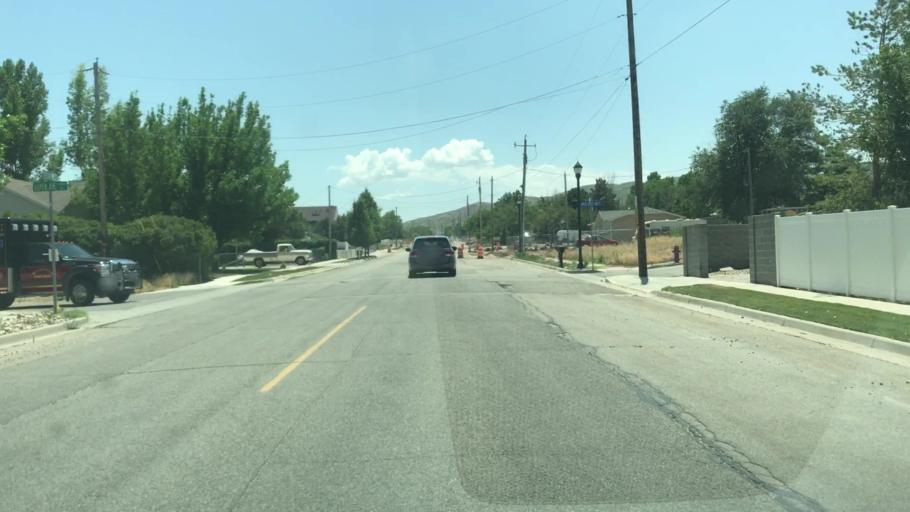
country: US
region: Utah
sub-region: Salt Lake County
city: Bluffdale
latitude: 40.4826
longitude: -111.9484
